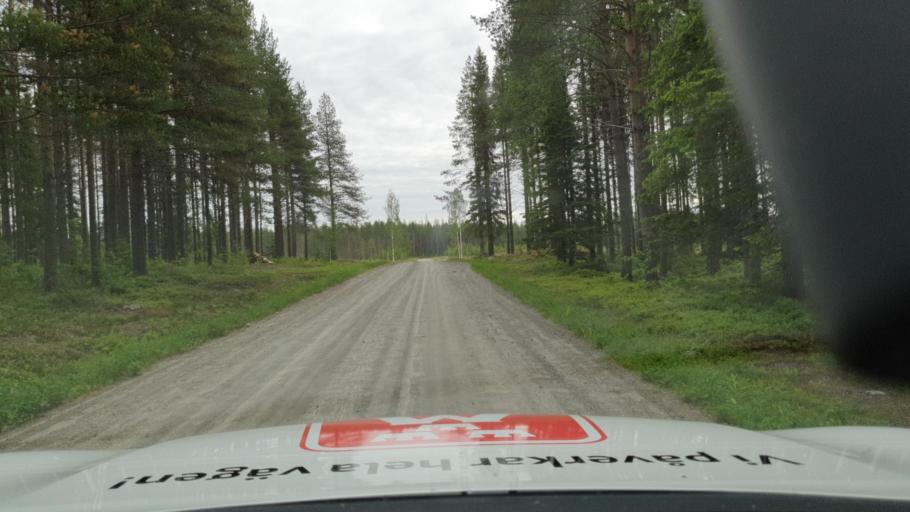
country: SE
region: Vaesterbotten
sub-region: Skelleftea Kommun
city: Langsele
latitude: 64.4770
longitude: 20.2107
